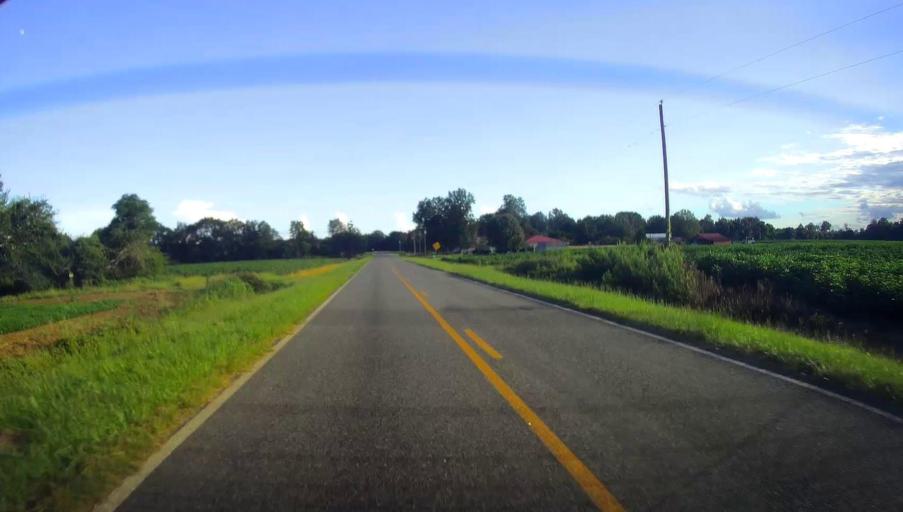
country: US
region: Georgia
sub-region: Pulaski County
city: Hawkinsville
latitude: 32.2768
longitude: -83.5386
